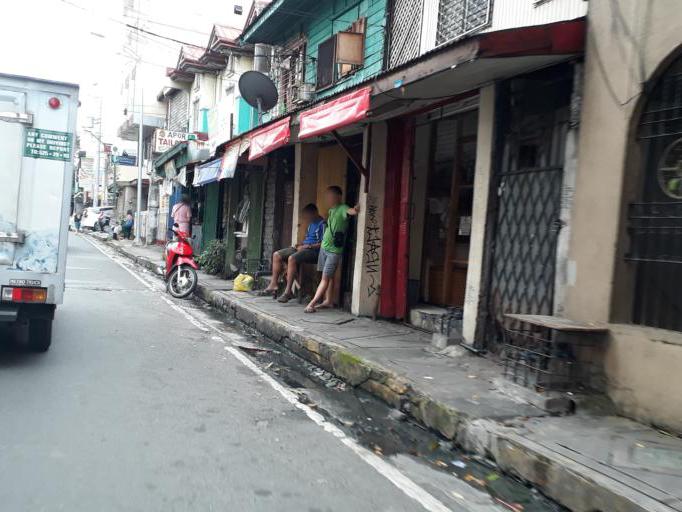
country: PH
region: Metro Manila
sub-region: City of Manila
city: Manila
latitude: 14.6088
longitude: 121.0038
